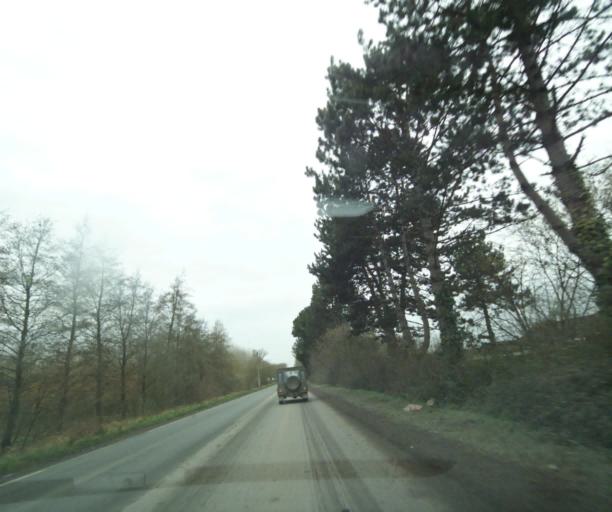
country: FR
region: Nord-Pas-de-Calais
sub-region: Departement du Nord
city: Vicq
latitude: 50.4055
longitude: 3.5939
